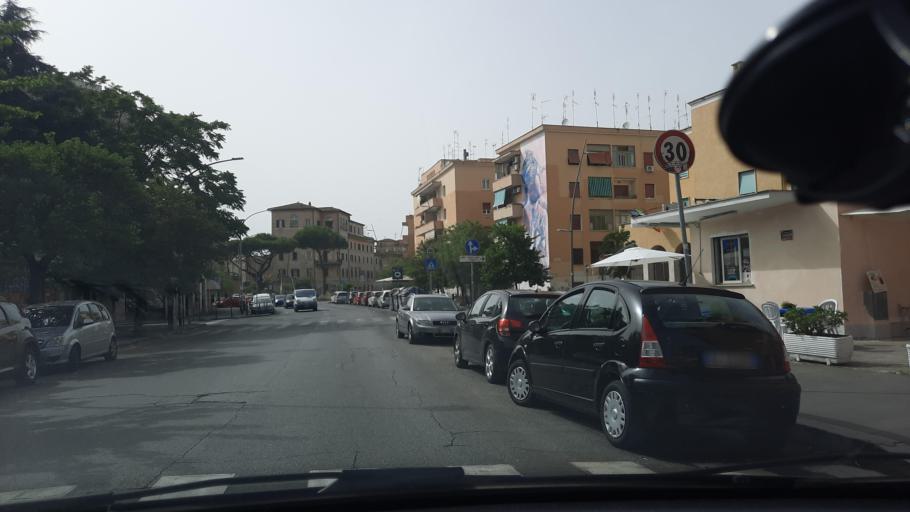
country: IT
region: Latium
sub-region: Citta metropolitana di Roma Capitale
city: Rome
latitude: 41.8604
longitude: 12.4872
